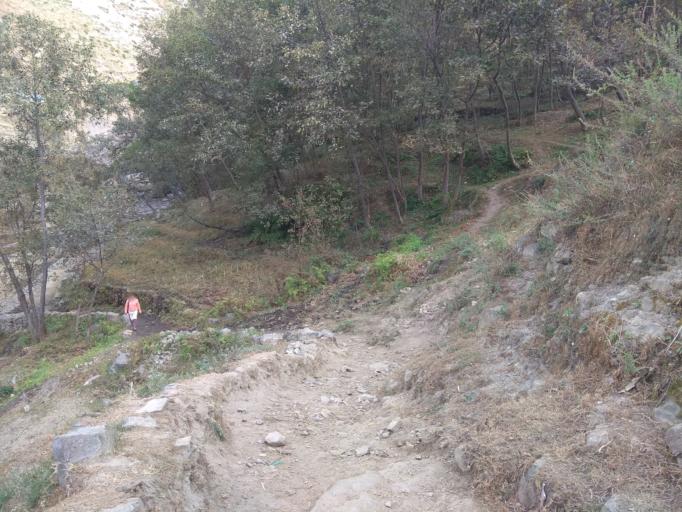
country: NP
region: Far Western
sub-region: Seti Zone
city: Achham
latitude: 29.2445
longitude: 81.6290
